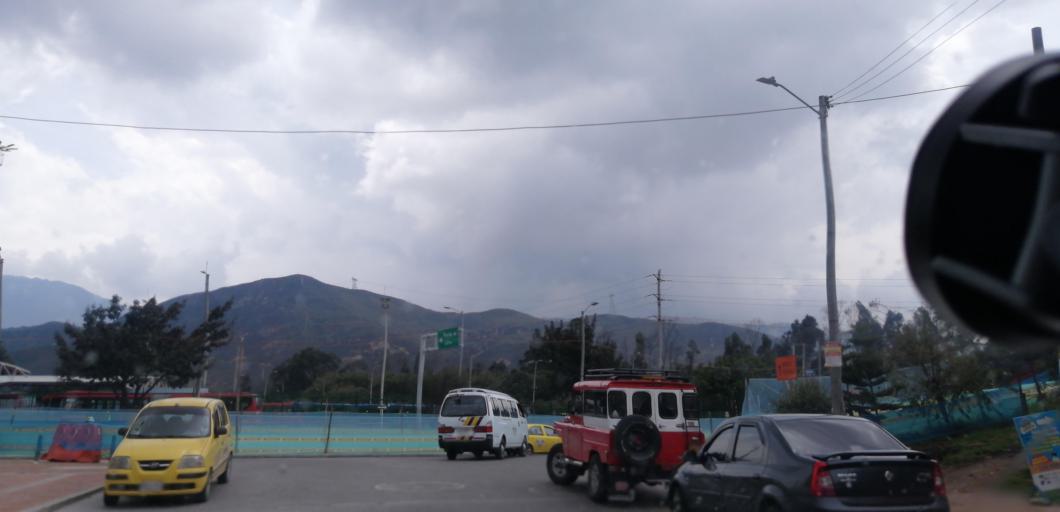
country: CO
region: Bogota D.C.
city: Bogota
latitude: 4.5331
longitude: -74.1189
